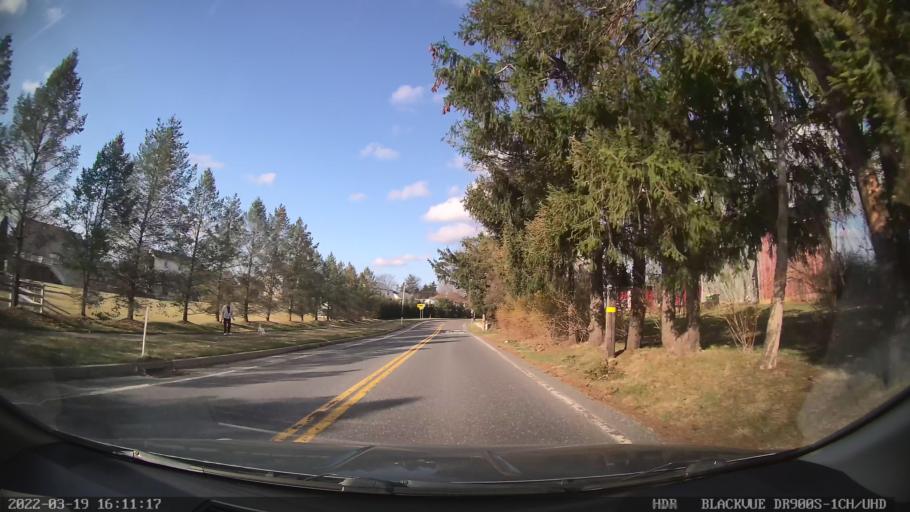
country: US
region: Pennsylvania
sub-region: Lehigh County
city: Wescosville
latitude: 40.5518
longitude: -75.5560
